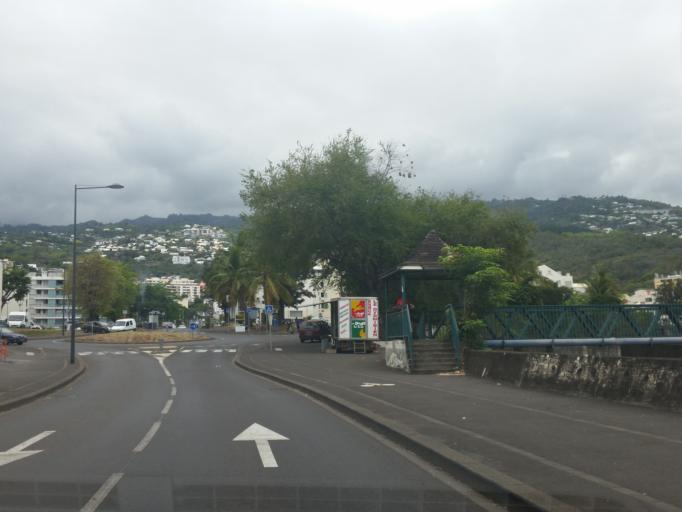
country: RE
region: Reunion
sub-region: Reunion
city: Saint-Denis
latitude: -20.8917
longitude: 55.4609
